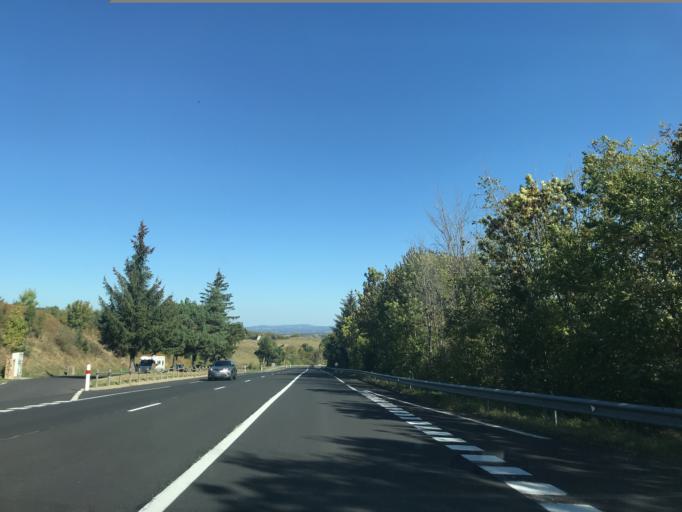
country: FR
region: Auvergne
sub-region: Departement du Puy-de-Dome
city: La Bourboule
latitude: 45.6709
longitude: 2.7874
